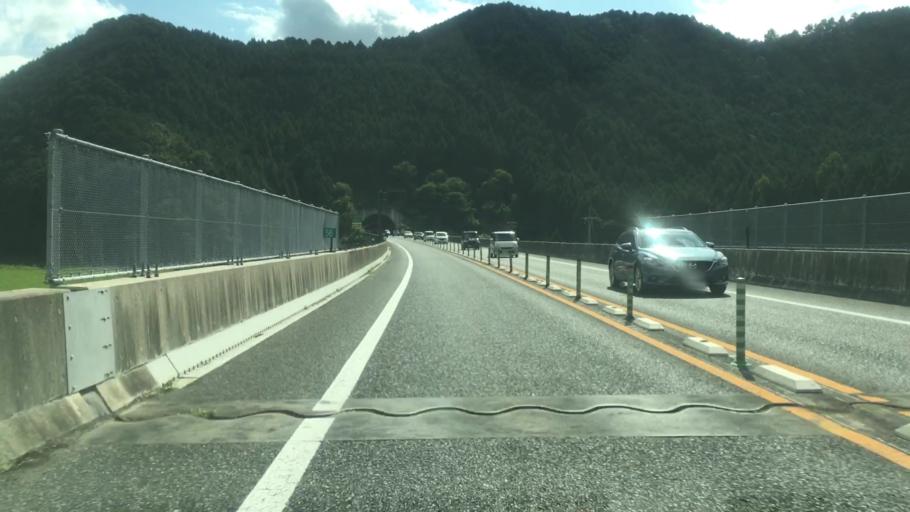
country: JP
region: Kyoto
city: Fukuchiyama
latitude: 35.2305
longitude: 135.0235
